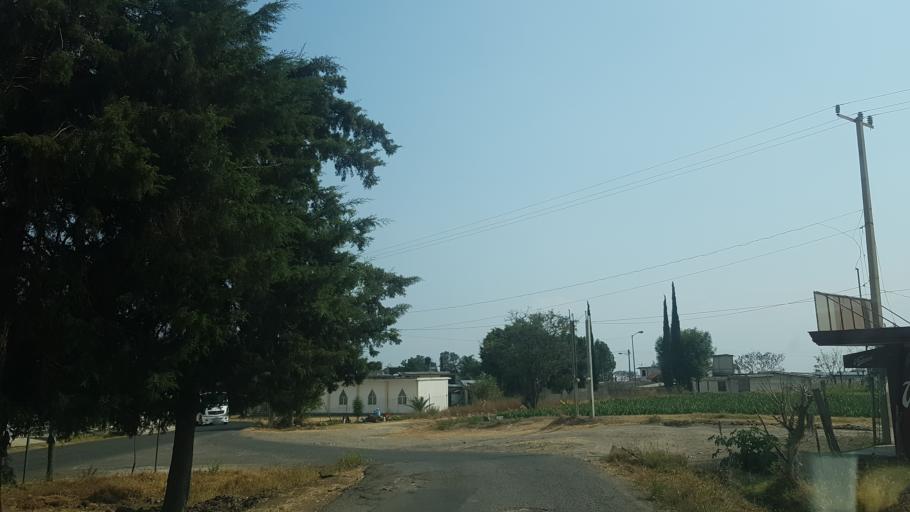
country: MX
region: Puebla
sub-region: Santa Isabel Cholula
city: Santa Ana Acozautla
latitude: 18.9491
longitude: -98.3954
